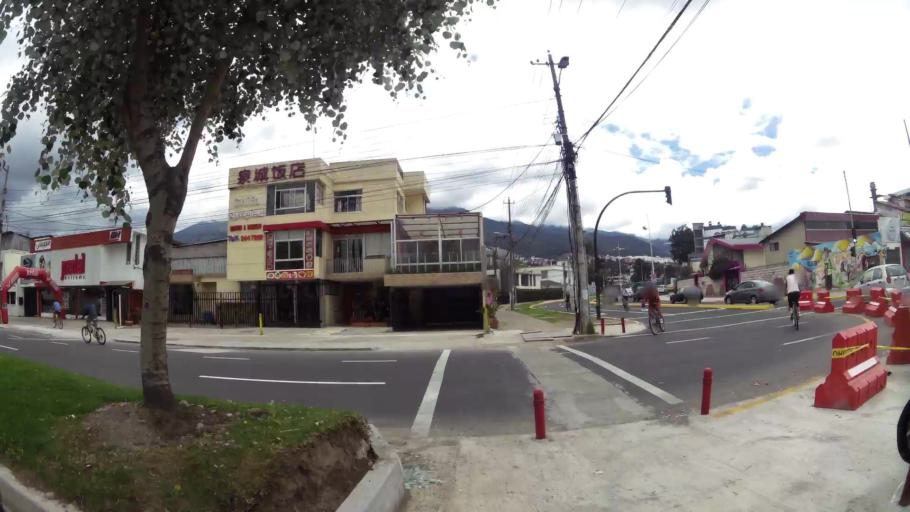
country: EC
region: Pichincha
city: Quito
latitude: -0.1658
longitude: -78.4839
